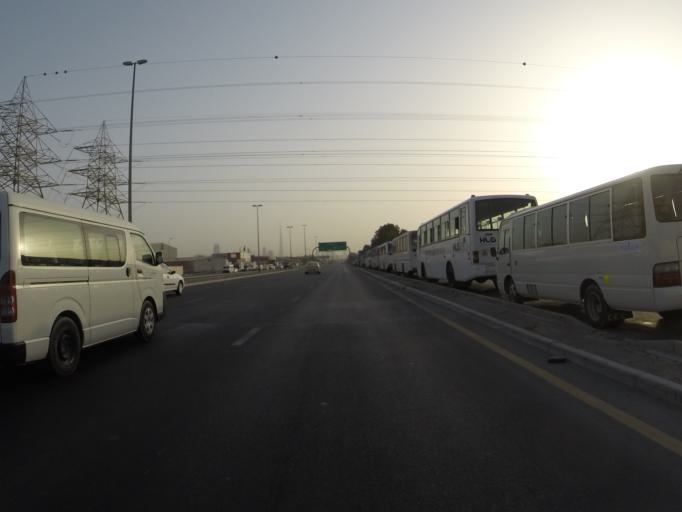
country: AE
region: Dubai
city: Dubai
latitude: 25.1361
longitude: 55.2377
